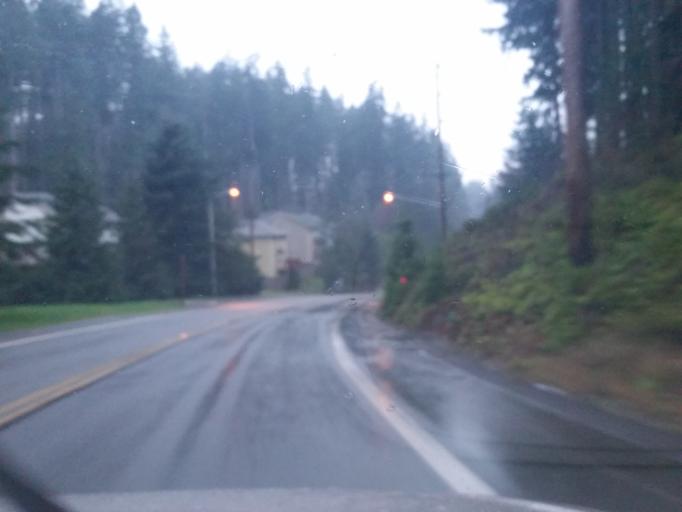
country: US
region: Washington
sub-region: Snohomish County
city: Meadowdale
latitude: 47.8741
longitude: -122.3113
